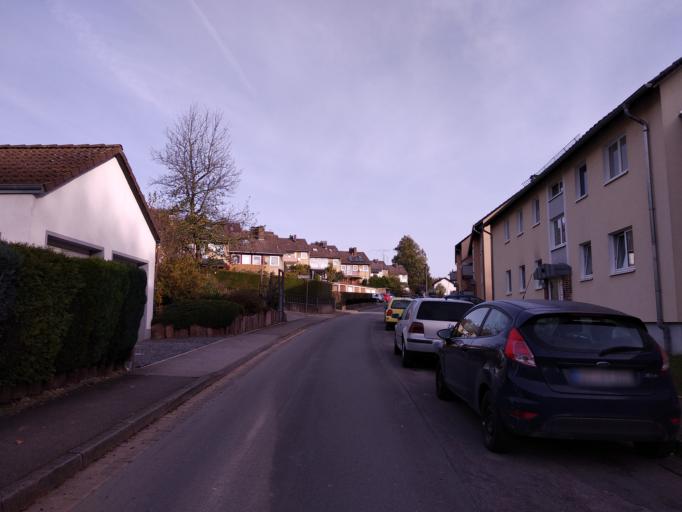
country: DE
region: North Rhine-Westphalia
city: Beverungen
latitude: 51.6738
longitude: 9.3716
